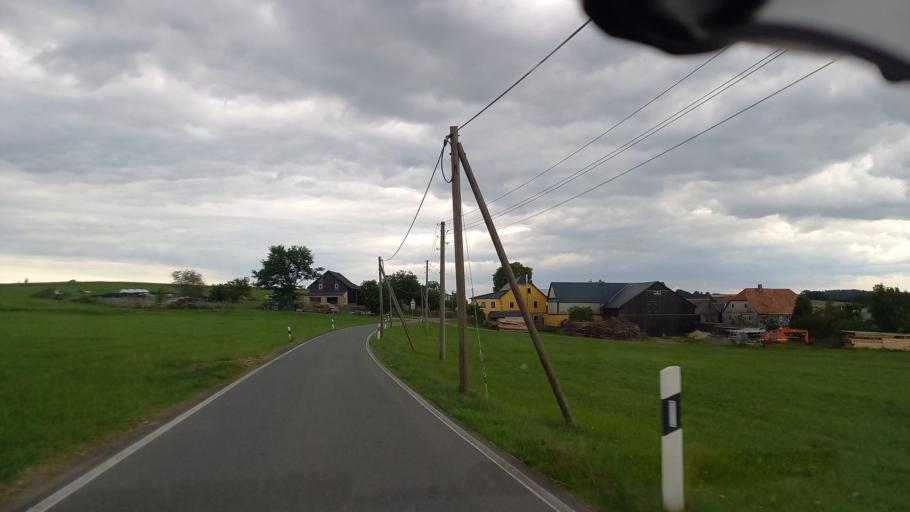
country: DE
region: Saxony
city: Rodewisch
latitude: 50.5777
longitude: 12.4432
